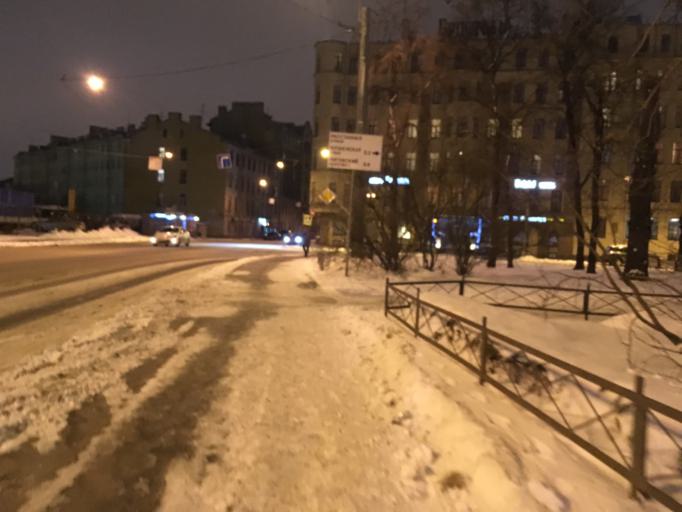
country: RU
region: St.-Petersburg
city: Centralniy
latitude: 59.9087
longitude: 30.3393
